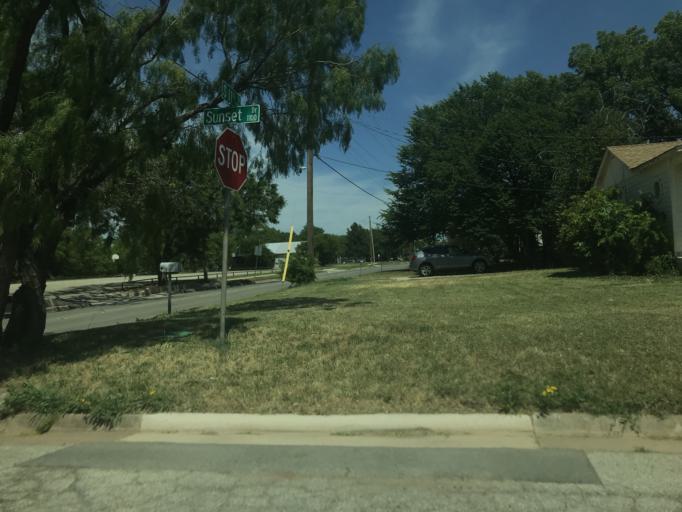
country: US
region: Texas
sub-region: Taylor County
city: Abilene
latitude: 32.4374
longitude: -99.7614
